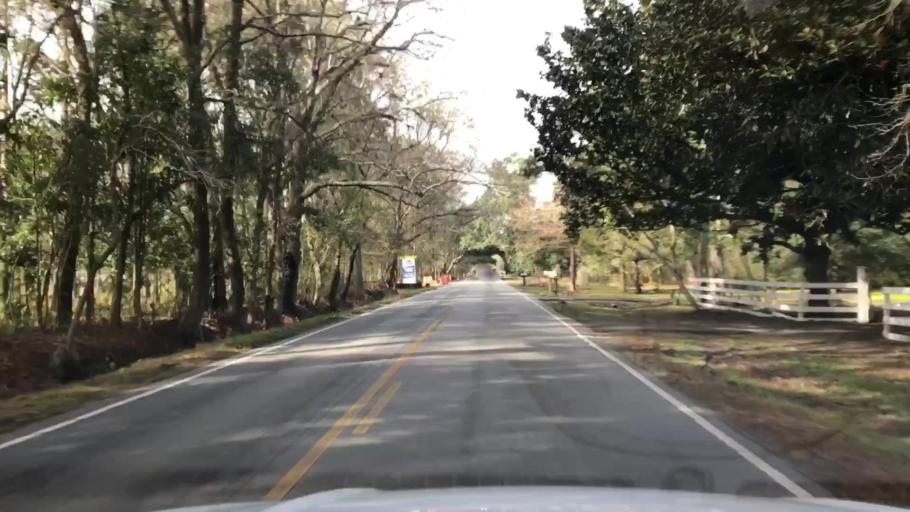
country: US
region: South Carolina
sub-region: Charleston County
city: Shell Point
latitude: 32.7657
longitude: -80.0660
